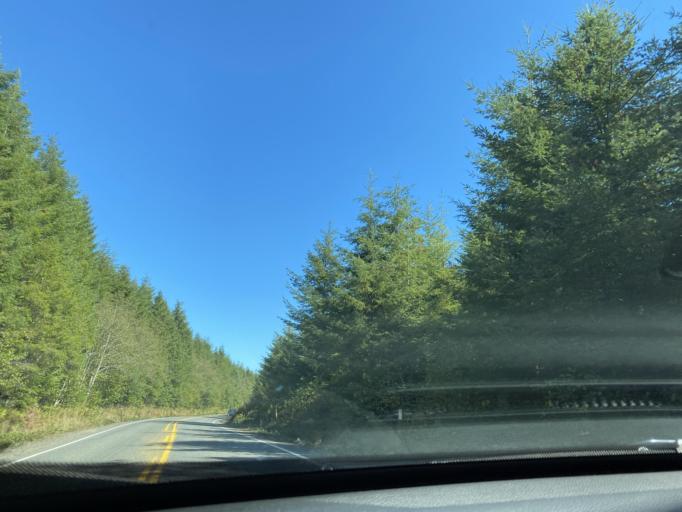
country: US
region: Washington
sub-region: Clallam County
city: Forks
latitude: 47.9330
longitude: -124.4776
